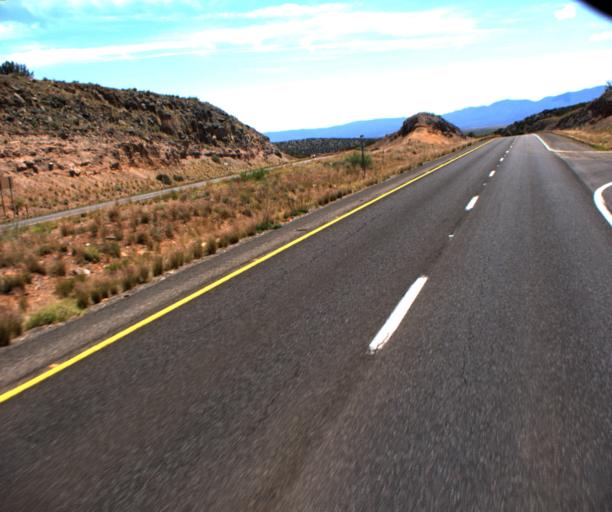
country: US
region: Arizona
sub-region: Yavapai County
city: Cornville
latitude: 34.8061
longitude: -111.9107
